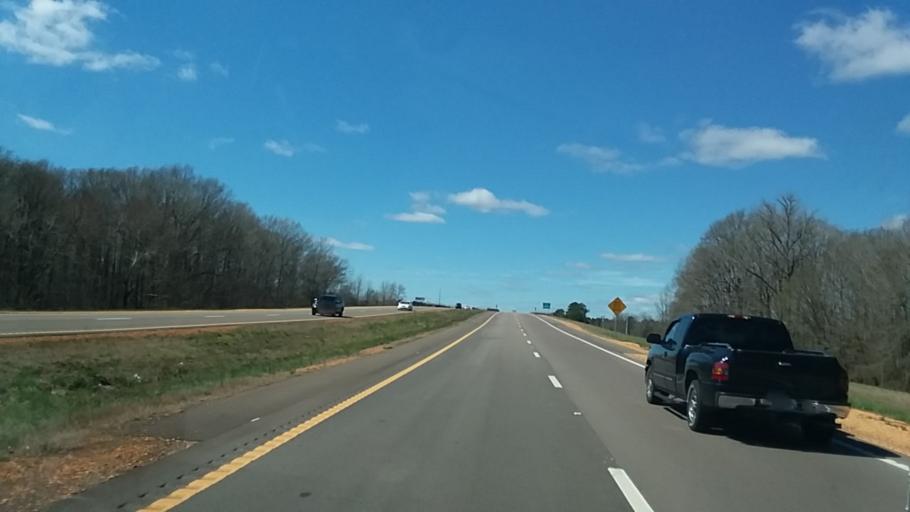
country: US
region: Mississippi
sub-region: Tishomingo County
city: Iuka
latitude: 34.8255
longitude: -88.2990
